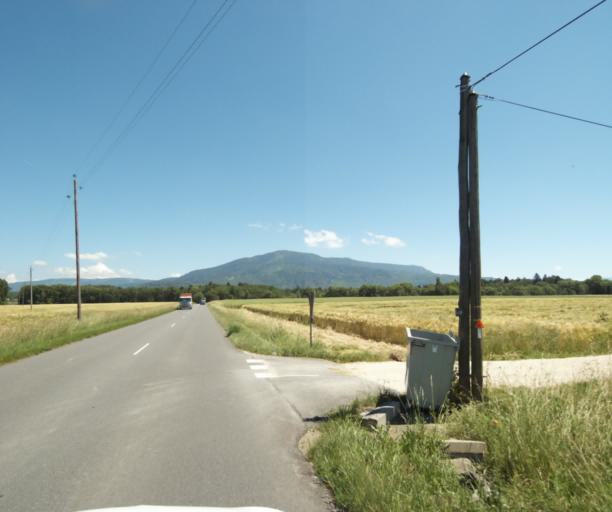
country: FR
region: Rhone-Alpes
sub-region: Departement de la Haute-Savoie
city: Loisin
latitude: 46.2686
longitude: 6.2930
